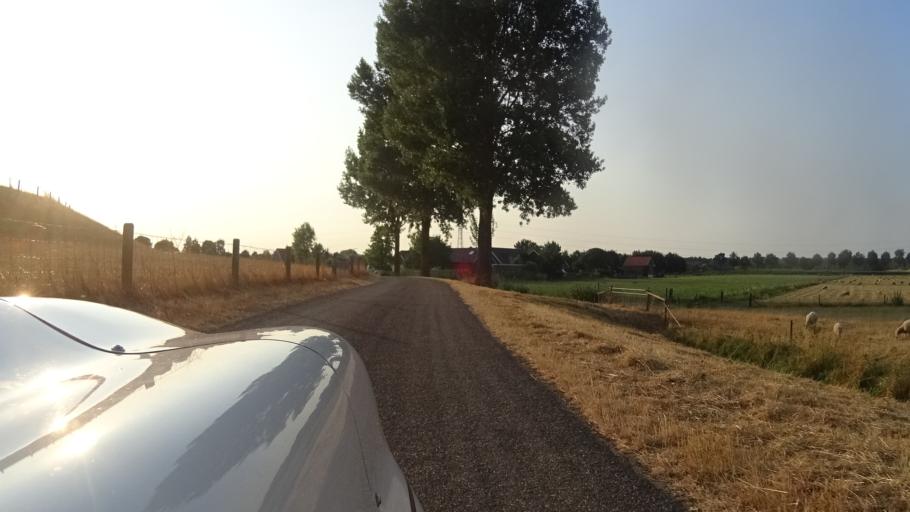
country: NL
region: Gelderland
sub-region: Gemeente Buren
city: Lienden
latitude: 51.9007
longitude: 5.4893
